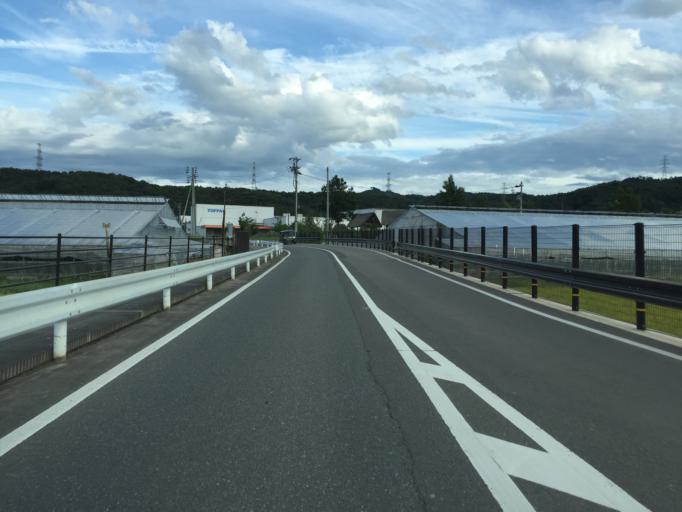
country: JP
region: Fukushima
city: Hobaramachi
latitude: 37.7915
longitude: 140.5144
